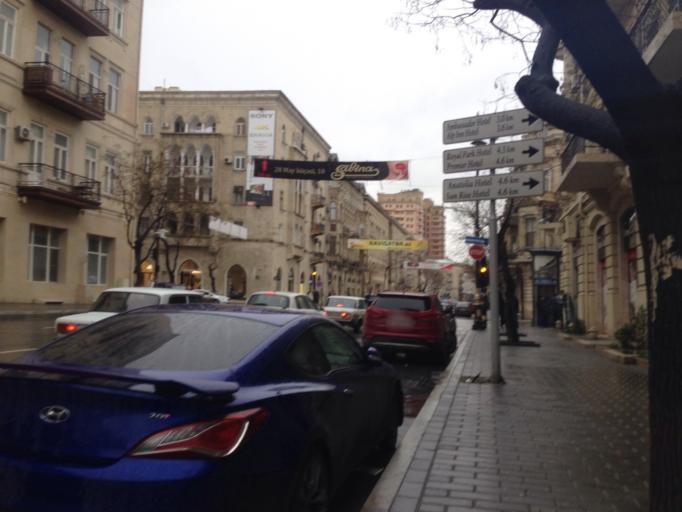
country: AZ
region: Baki
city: Baku
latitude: 40.3760
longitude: 49.8463
